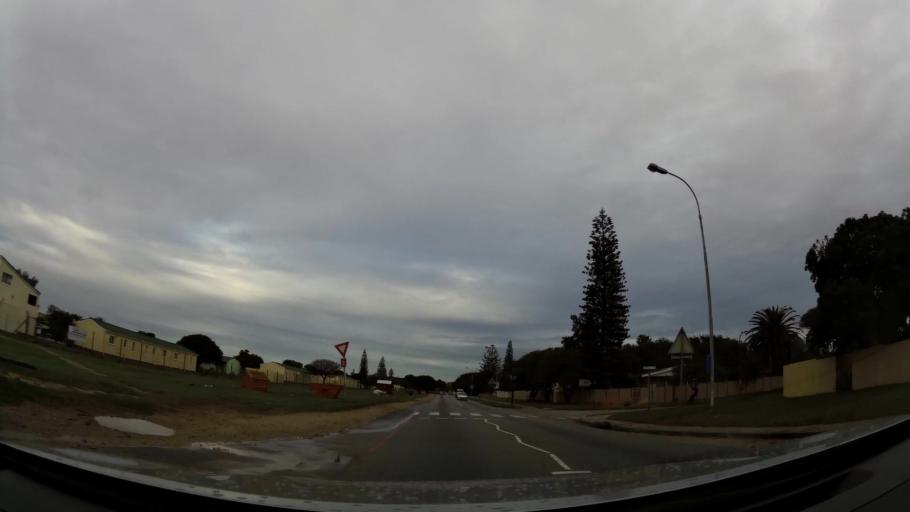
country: ZA
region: Eastern Cape
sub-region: Nelson Mandela Bay Metropolitan Municipality
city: Port Elizabeth
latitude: -33.9871
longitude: 25.5526
